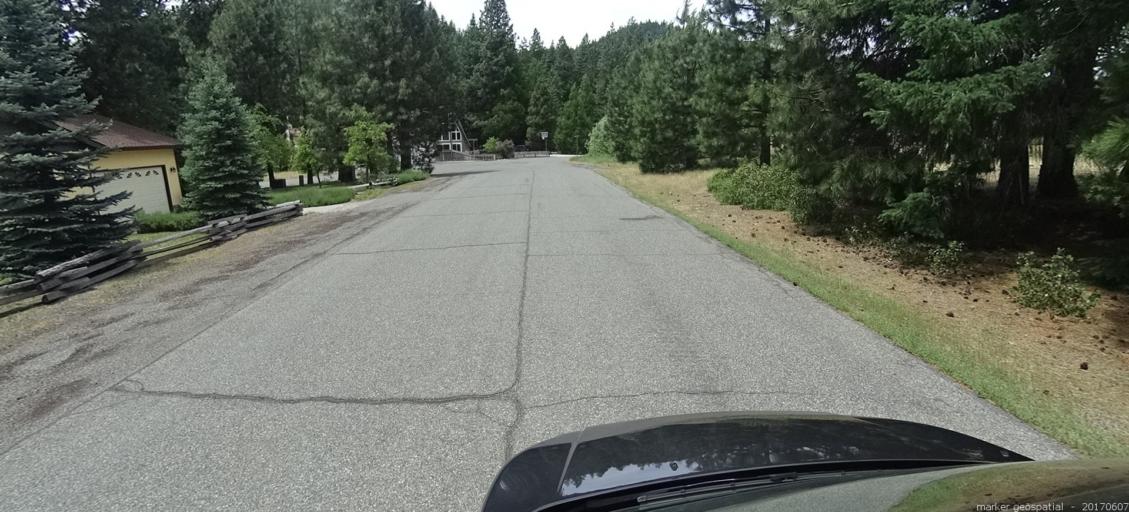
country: US
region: California
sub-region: Siskiyou County
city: Mount Shasta
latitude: 41.2924
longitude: -122.3228
